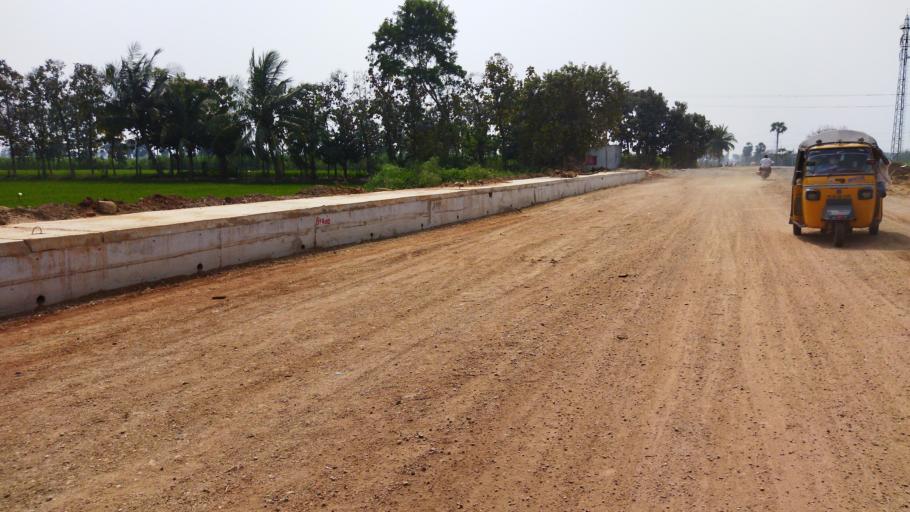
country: IN
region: Telangana
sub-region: Nalgonda
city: Nalgonda
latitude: 17.1216
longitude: 79.3658
